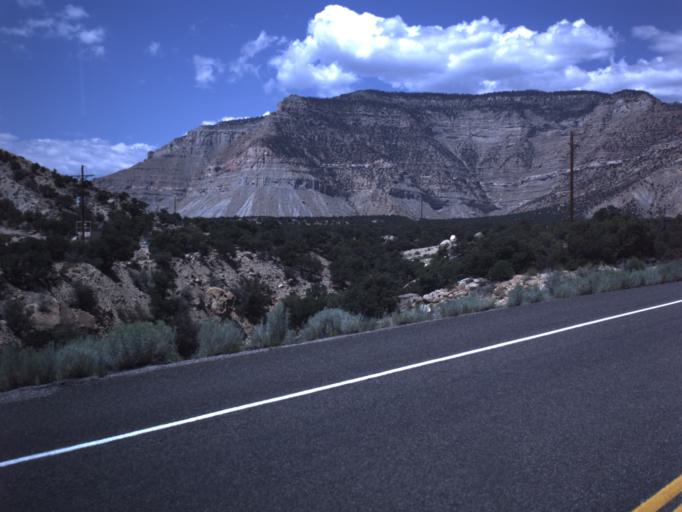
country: US
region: Utah
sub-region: Emery County
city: Orangeville
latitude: 39.2839
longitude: -111.1052
